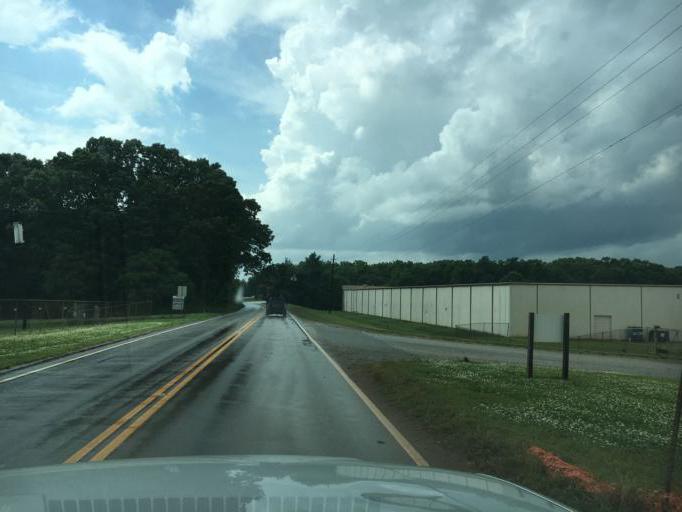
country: US
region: South Carolina
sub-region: Spartanburg County
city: Wellford
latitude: 34.9332
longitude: -82.0644
